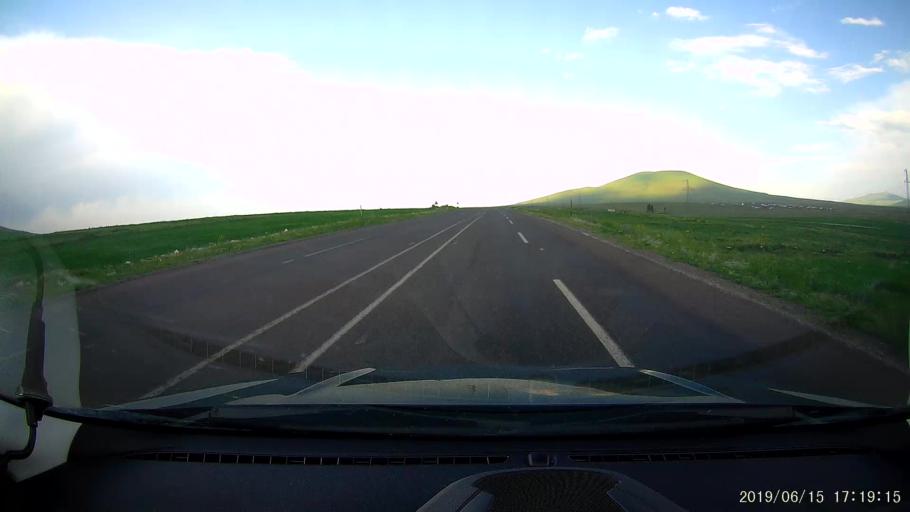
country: TR
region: Kars
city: Kars
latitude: 40.6164
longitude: 43.2742
